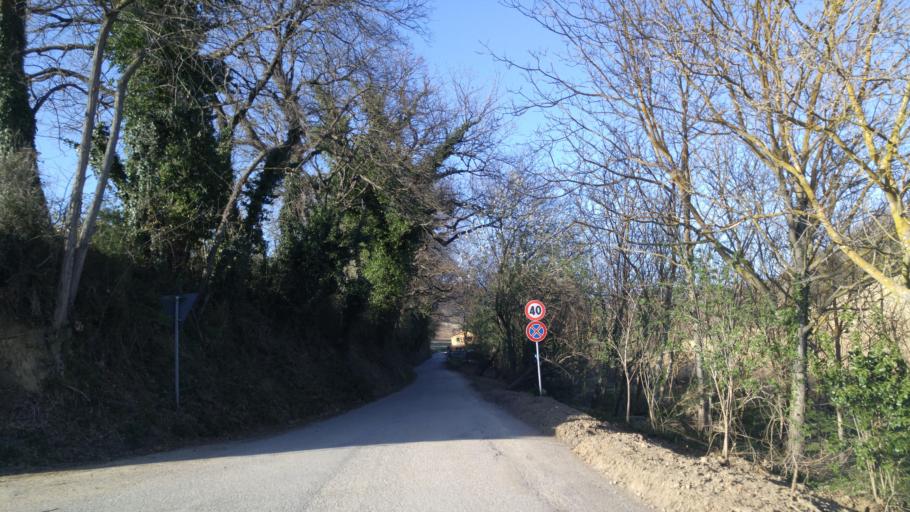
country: IT
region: The Marches
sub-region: Provincia di Pesaro e Urbino
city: Fenile
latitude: 43.8384
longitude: 12.9141
